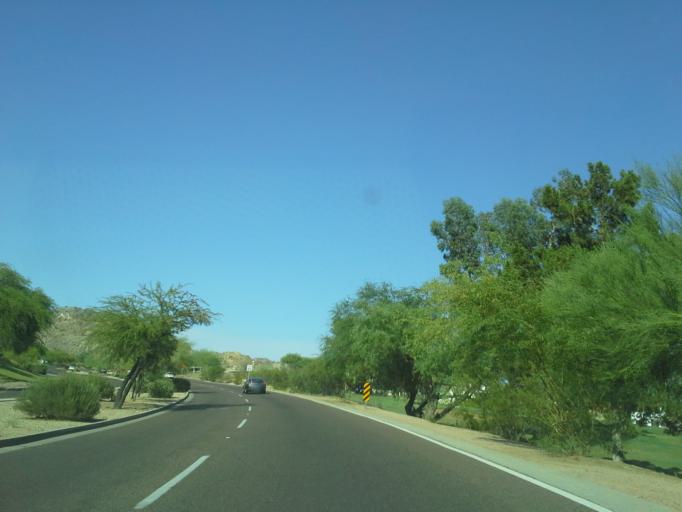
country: US
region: Arizona
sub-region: Maricopa County
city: Paradise Valley
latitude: 33.5295
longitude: -112.0174
